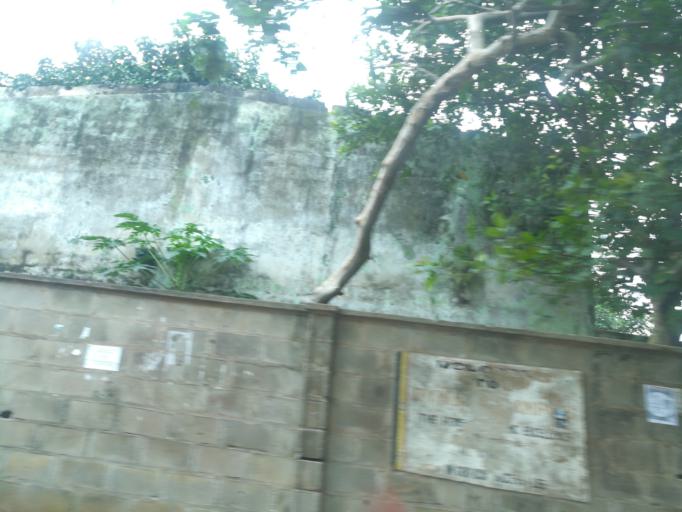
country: NG
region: Lagos
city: Oshodi
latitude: 6.5687
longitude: 3.3517
